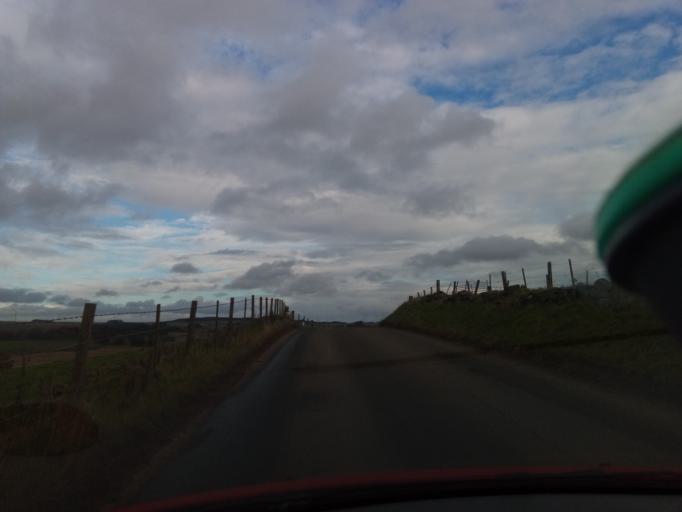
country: GB
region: Scotland
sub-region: South Lanarkshire
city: Carnwath
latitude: 55.7727
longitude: -3.6006
